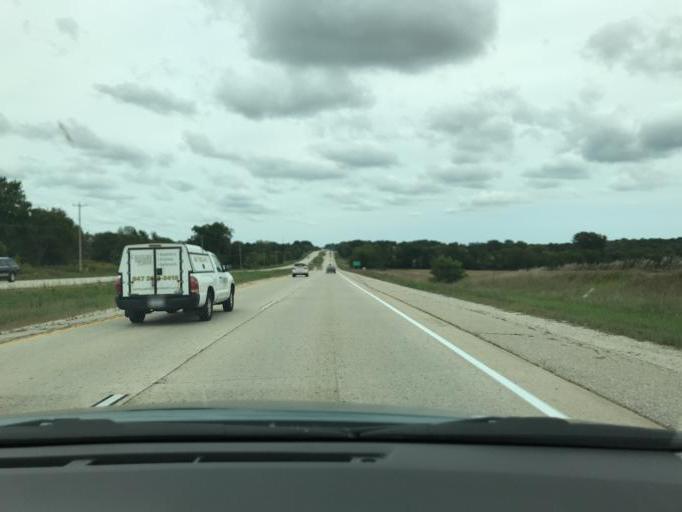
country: US
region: Wisconsin
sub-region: Kenosha County
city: Paddock Lake
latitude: 42.5680
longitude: -88.0896
